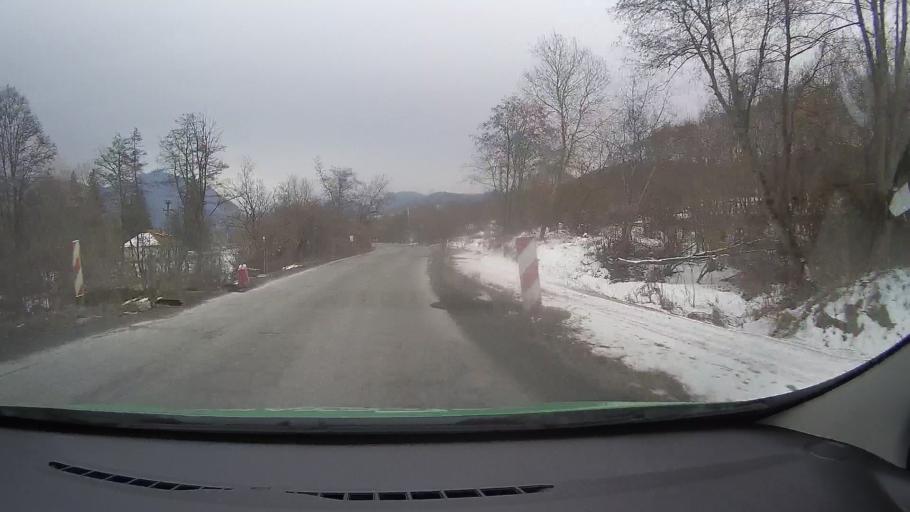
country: RO
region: Brasov
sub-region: Oras Rasnov
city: Rasnov
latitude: 45.5568
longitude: 25.4731
